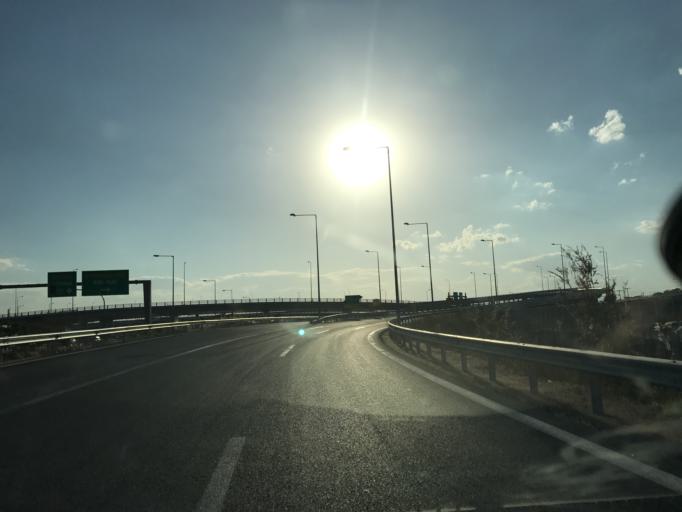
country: GR
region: Central Macedonia
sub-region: Nomos Thessalonikis
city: Menemeni
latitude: 40.6557
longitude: 22.8843
